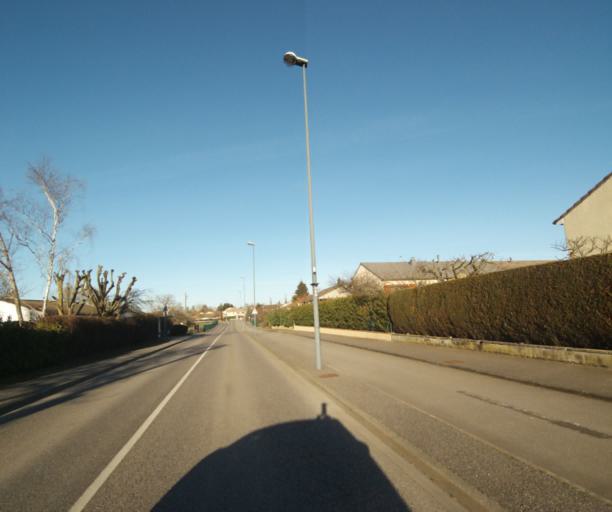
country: FR
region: Lorraine
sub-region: Departement de Meurthe-et-Moselle
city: Seichamps
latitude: 48.7125
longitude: 6.2675
